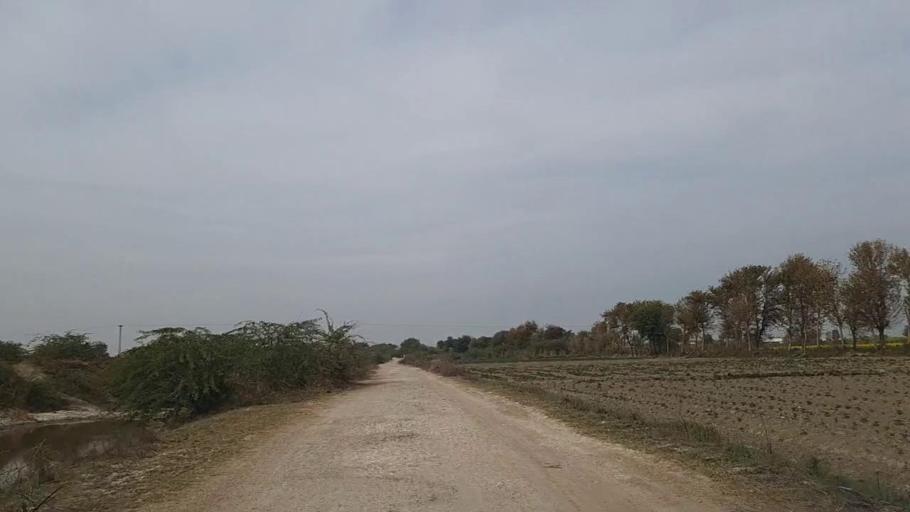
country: PK
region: Sindh
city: Daur
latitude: 26.4222
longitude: 68.4189
